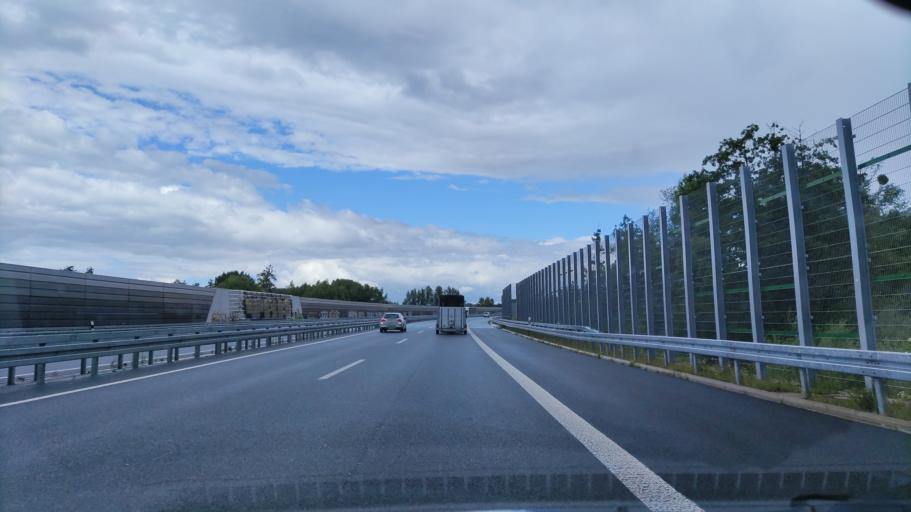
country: DE
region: North Rhine-Westphalia
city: Bad Oeynhausen
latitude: 52.2133
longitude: 8.7560
